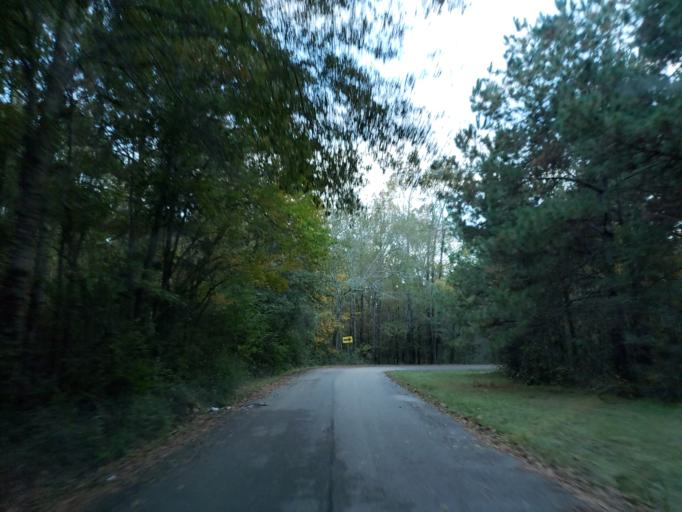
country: US
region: Mississippi
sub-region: Forrest County
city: Hattiesburg
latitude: 31.2816
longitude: -89.2543
